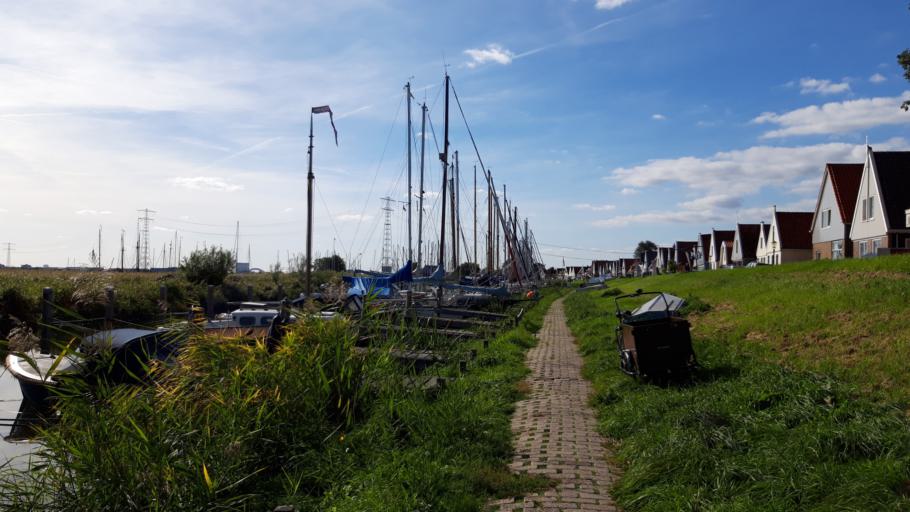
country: NL
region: North Holland
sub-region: Gemeente Diemen
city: Diemen
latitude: 52.3793
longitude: 4.9963
